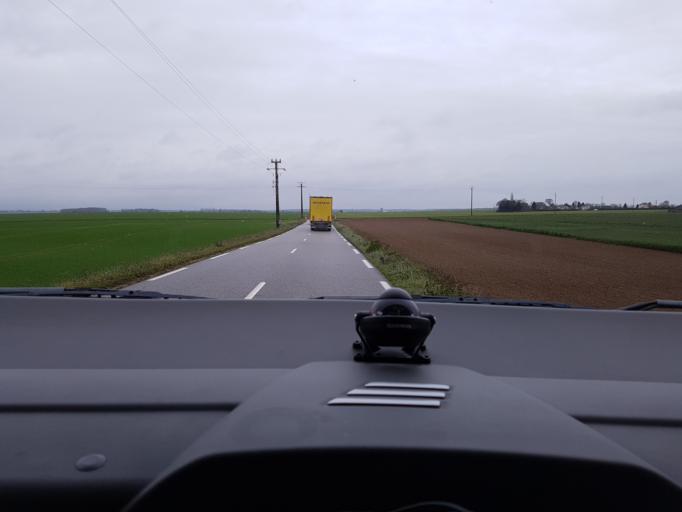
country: FR
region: Haute-Normandie
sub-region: Departement de l'Eure
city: Etrepagny
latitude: 49.3655
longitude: 1.5634
